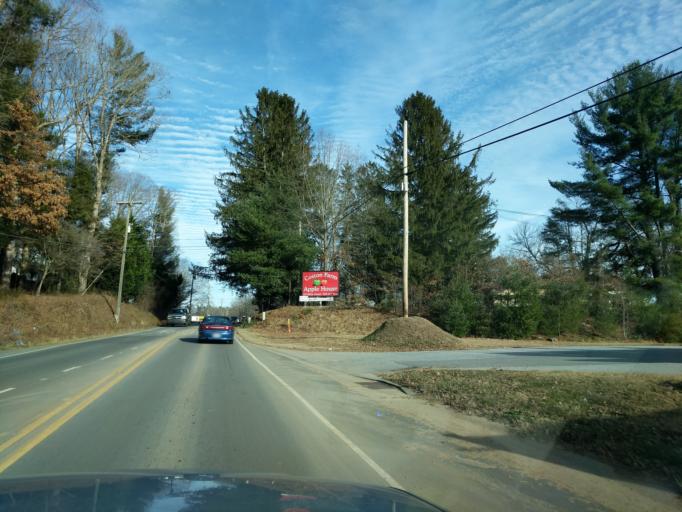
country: US
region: North Carolina
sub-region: Henderson County
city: Fruitland
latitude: 35.3599
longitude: -82.4179
